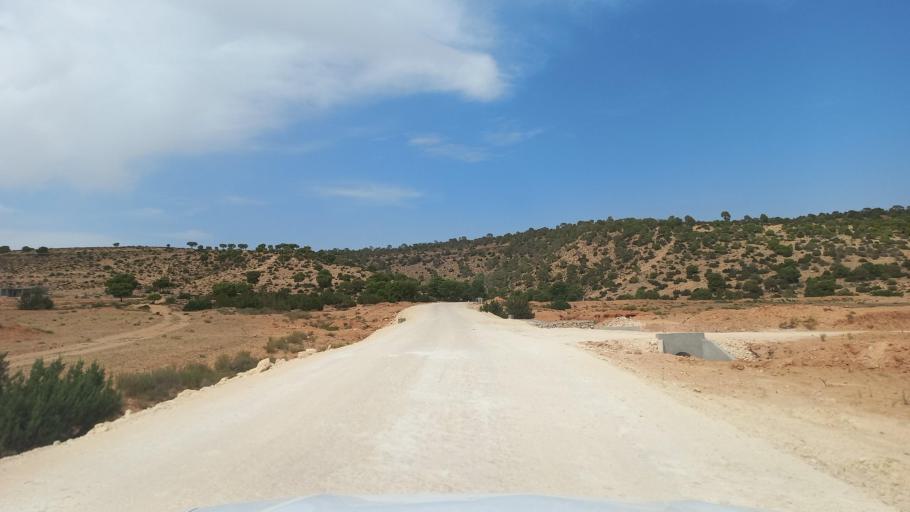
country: TN
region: Al Qasrayn
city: Kasserine
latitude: 35.3718
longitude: 8.8882
